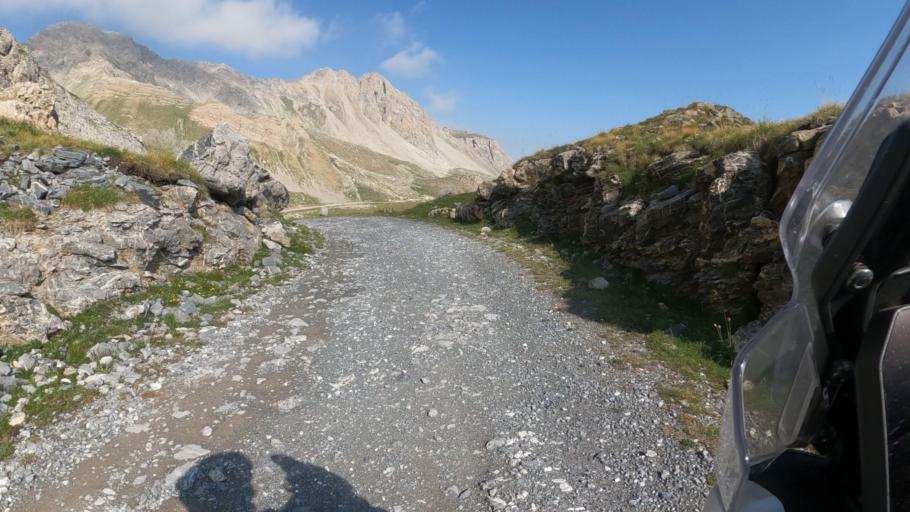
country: IT
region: Piedmont
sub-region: Provincia di Cuneo
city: Pietraporzio
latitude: 44.3861
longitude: 7.0343
